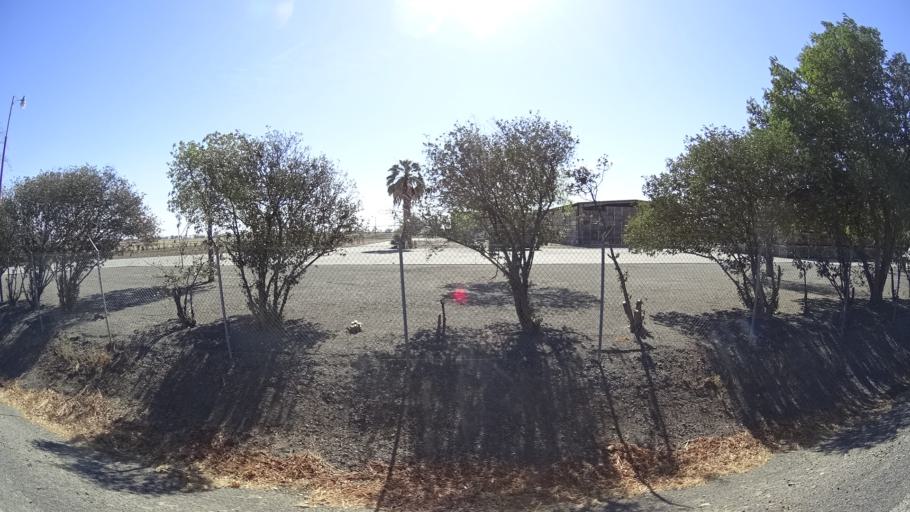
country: US
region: California
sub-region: Yolo County
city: Cottonwood
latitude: 38.6204
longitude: -121.9628
